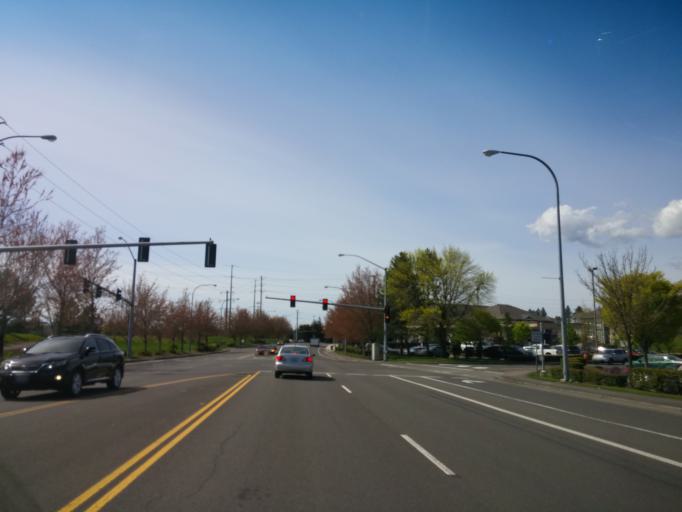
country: US
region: Oregon
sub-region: Washington County
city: Aloha
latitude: 45.5085
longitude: -122.8433
